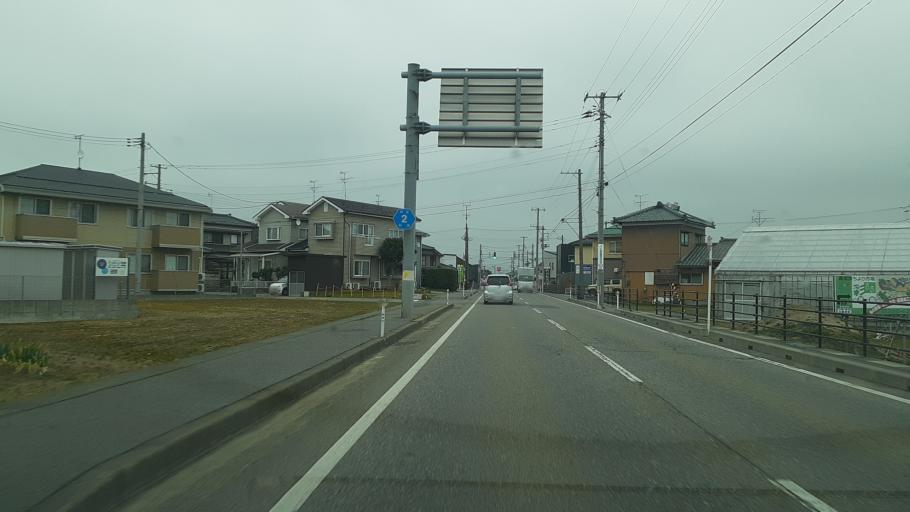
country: JP
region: Niigata
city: Niigata-shi
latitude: 37.8549
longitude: 139.0344
